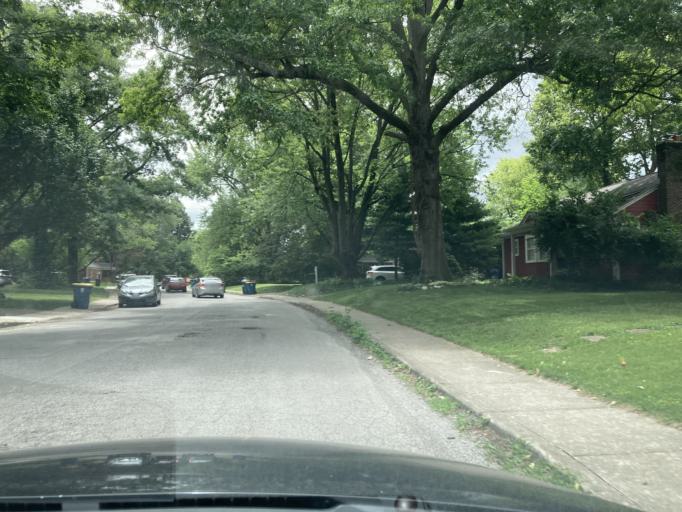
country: US
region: Indiana
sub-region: Marion County
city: Broad Ripple
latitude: 39.8526
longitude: -86.1330
